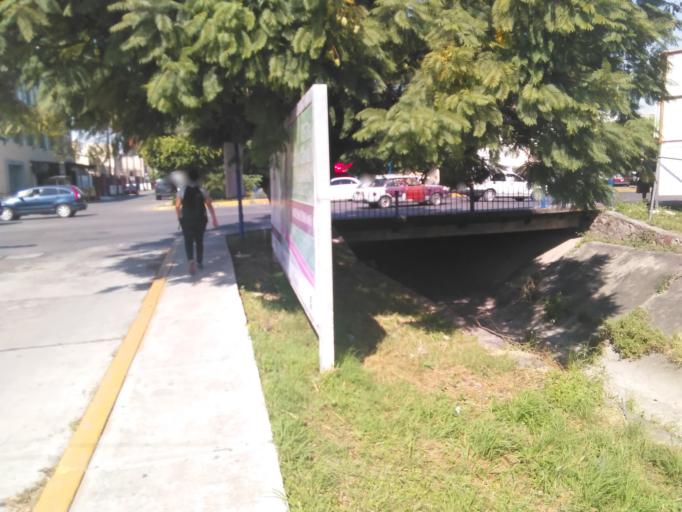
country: MX
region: Nayarit
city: Tepic
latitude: 21.4911
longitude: -104.8827
